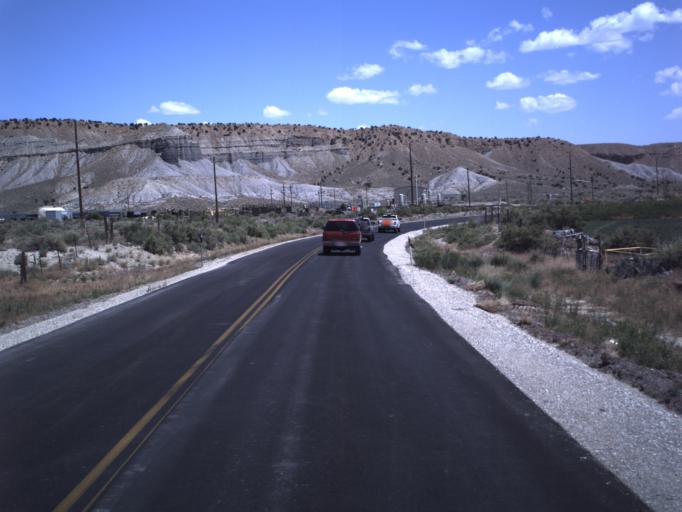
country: US
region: Utah
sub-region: Emery County
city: Orangeville
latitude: 39.2608
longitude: -111.1155
